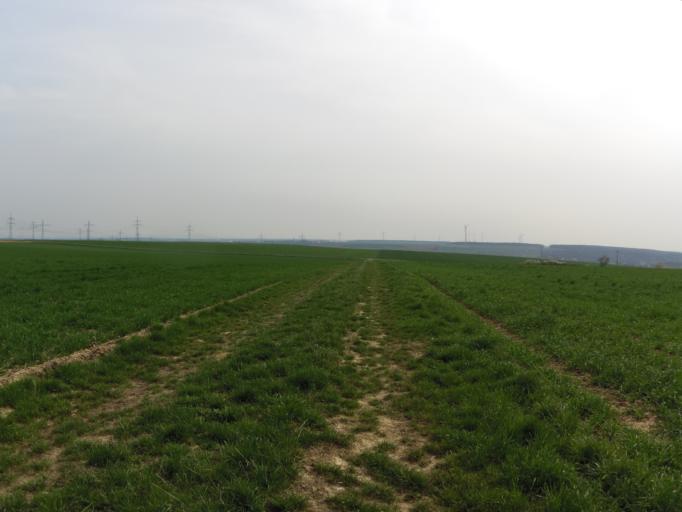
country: DE
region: Bavaria
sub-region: Regierungsbezirk Unterfranken
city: Theilheim
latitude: 49.7722
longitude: 10.0378
